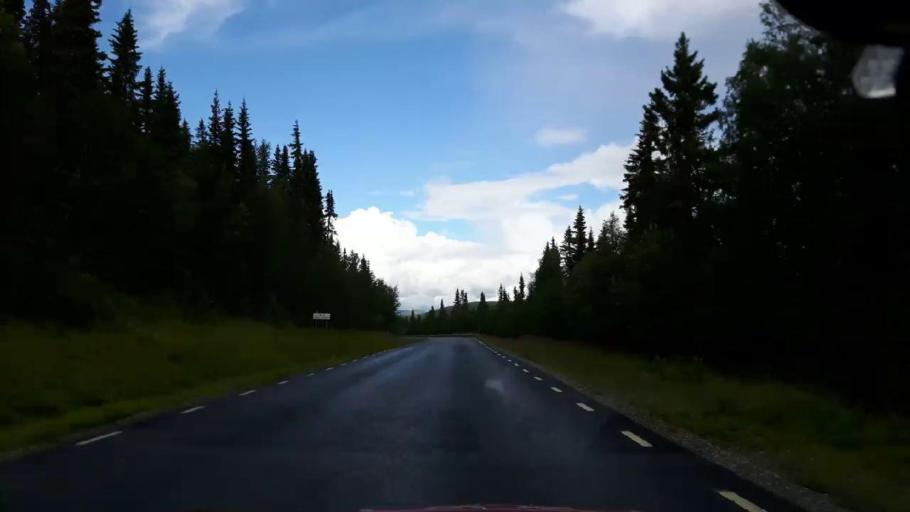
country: SE
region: Vaesterbotten
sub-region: Vilhelmina Kommun
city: Sjoberg
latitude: 64.9998
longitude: 15.1992
